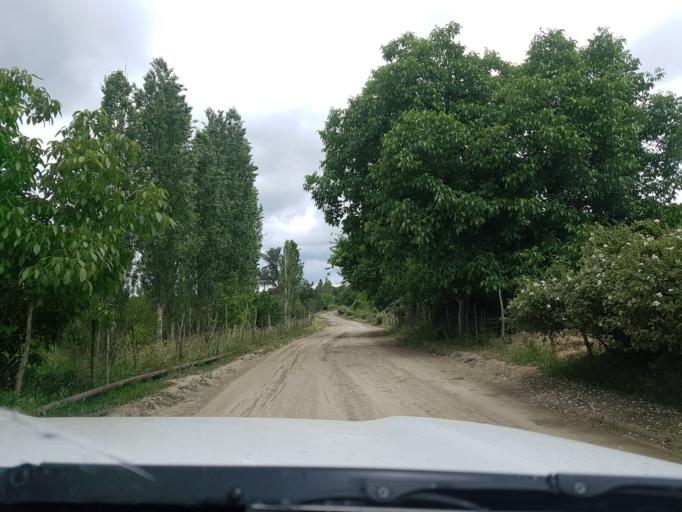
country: TM
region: Ahal
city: Baharly
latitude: 38.1963
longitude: 57.0045
